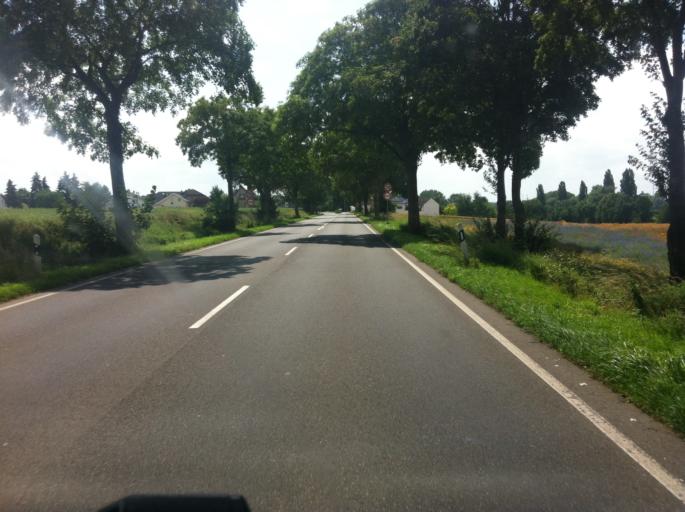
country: DE
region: North Rhine-Westphalia
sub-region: Regierungsbezirk Koln
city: Weilerswist
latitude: 50.7209
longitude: 6.8189
